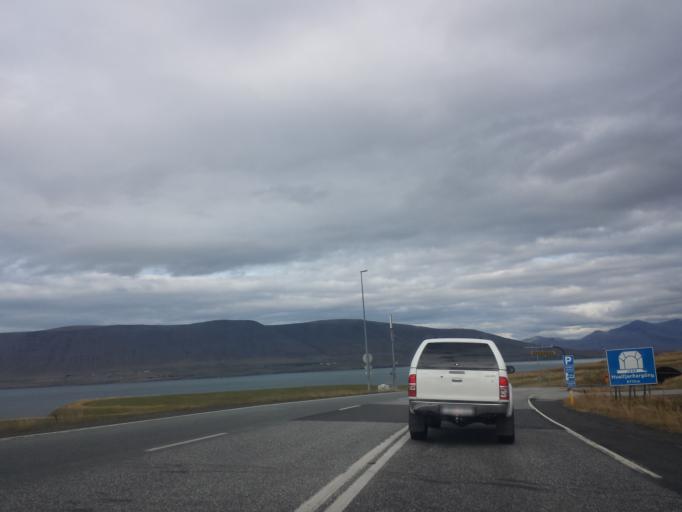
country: IS
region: Capital Region
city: Reykjavik
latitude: 64.2806
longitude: -21.8402
